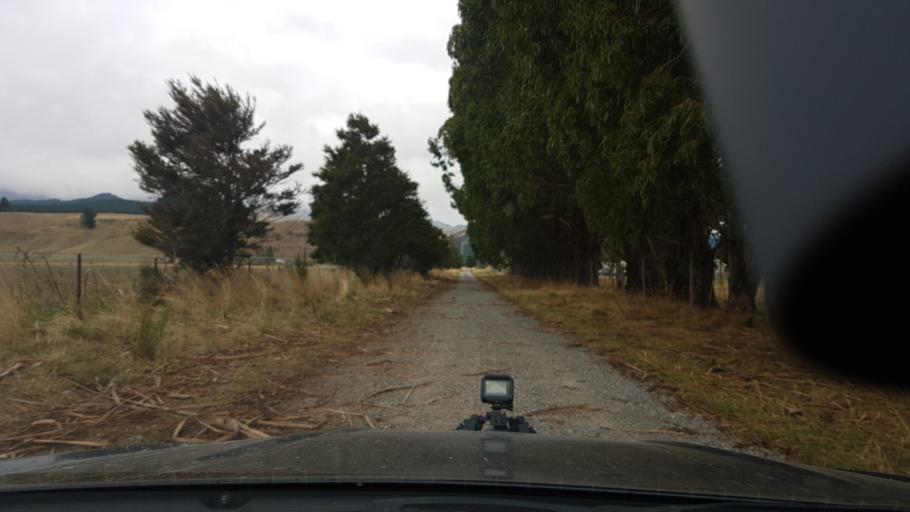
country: NZ
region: Tasman
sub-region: Tasman District
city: Brightwater
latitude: -41.6576
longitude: 173.2385
